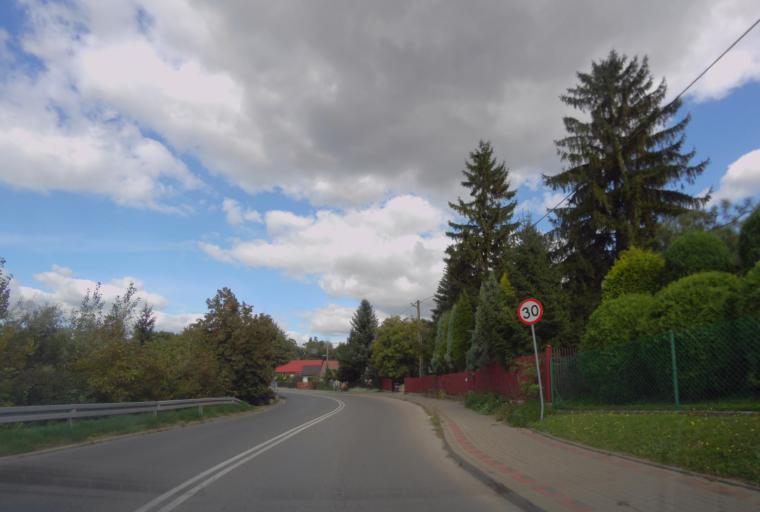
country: PL
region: Subcarpathian Voivodeship
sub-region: Tarnobrzeg
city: Tarnobrzeg
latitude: 50.5548
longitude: 21.6625
